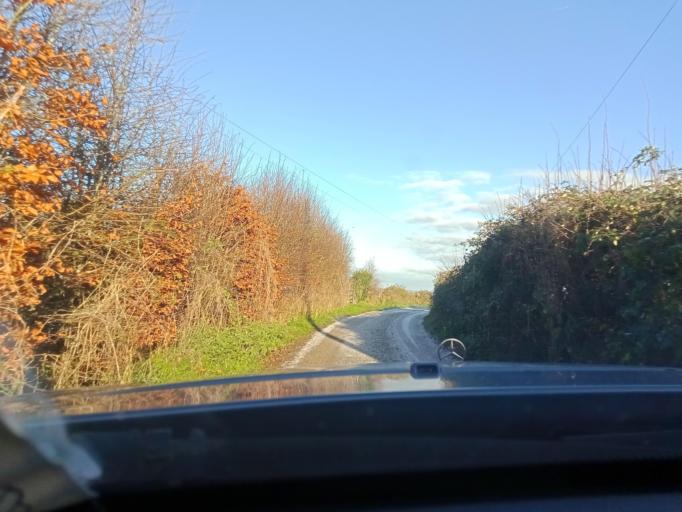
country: IE
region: Leinster
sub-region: Kilkenny
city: Graiguenamanagh
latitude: 52.5621
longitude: -6.9417
